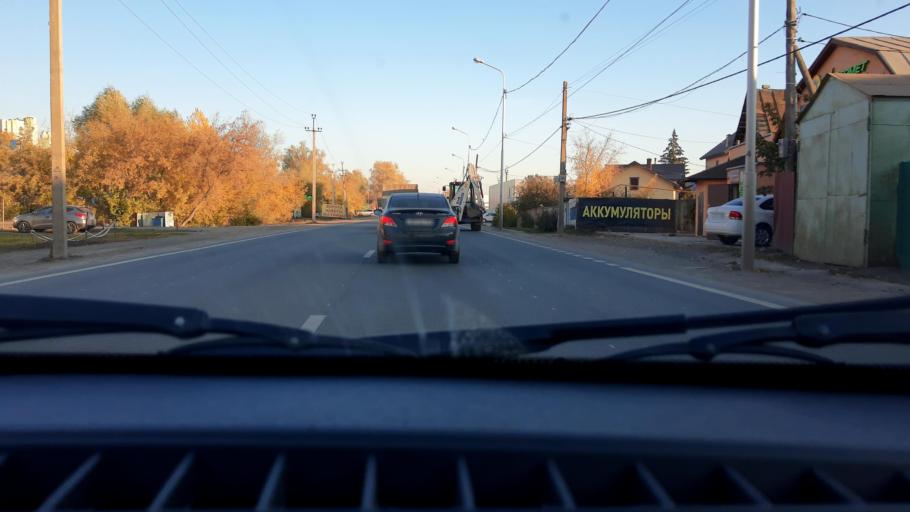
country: RU
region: Bashkortostan
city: Ufa
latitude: 54.6924
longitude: 55.9802
